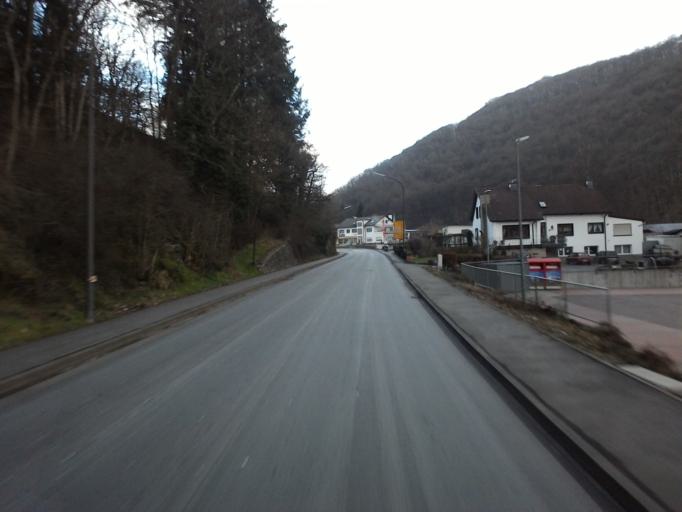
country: DE
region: Rheinland-Pfalz
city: Scheuern
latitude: 50.0190
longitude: 6.2885
